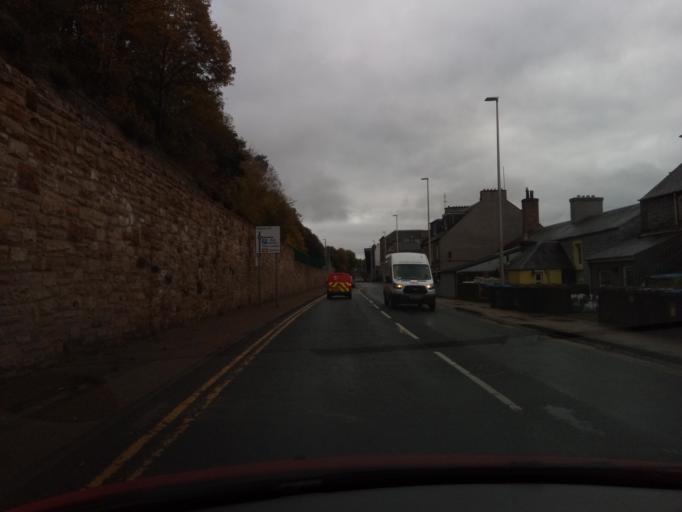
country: GB
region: Scotland
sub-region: The Scottish Borders
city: Galashiels
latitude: 55.6187
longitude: -2.8083
